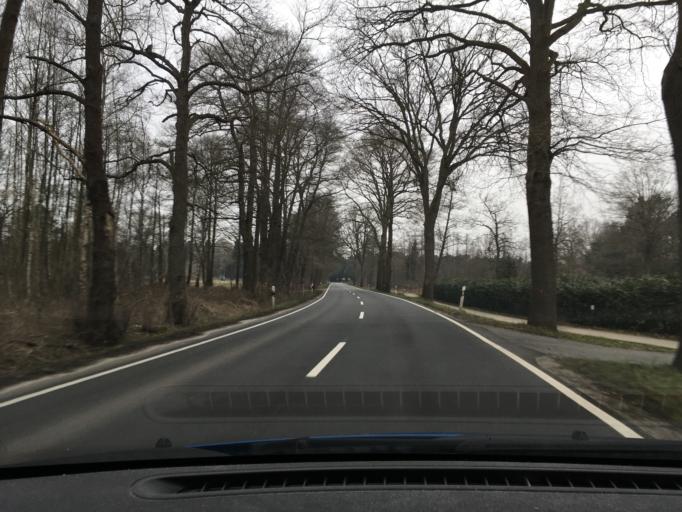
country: DE
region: Lower Saxony
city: Isernhagen Farster Bauerschaft
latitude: 52.5151
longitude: 9.8017
